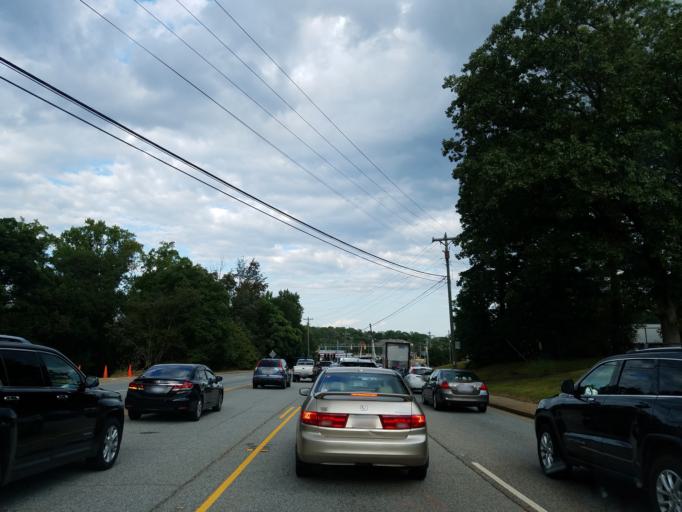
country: US
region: South Carolina
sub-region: Greenville County
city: Taylors
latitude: 34.8625
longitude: -82.2812
